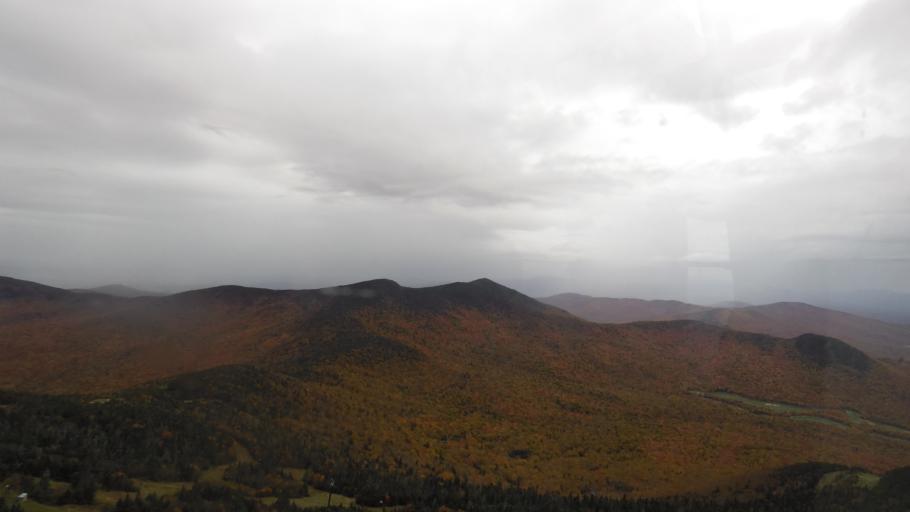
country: US
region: Vermont
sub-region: Franklin County
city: Richford
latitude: 44.9252
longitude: -72.5251
